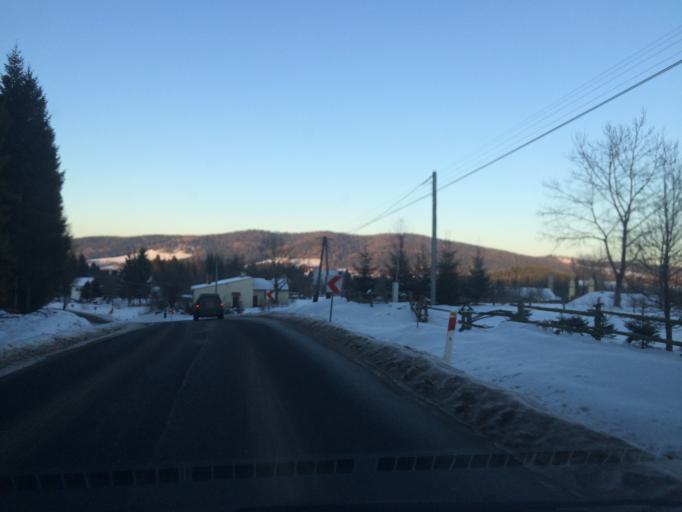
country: PL
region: Subcarpathian Voivodeship
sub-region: Powiat bieszczadzki
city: Czarna
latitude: 49.3064
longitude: 22.6721
